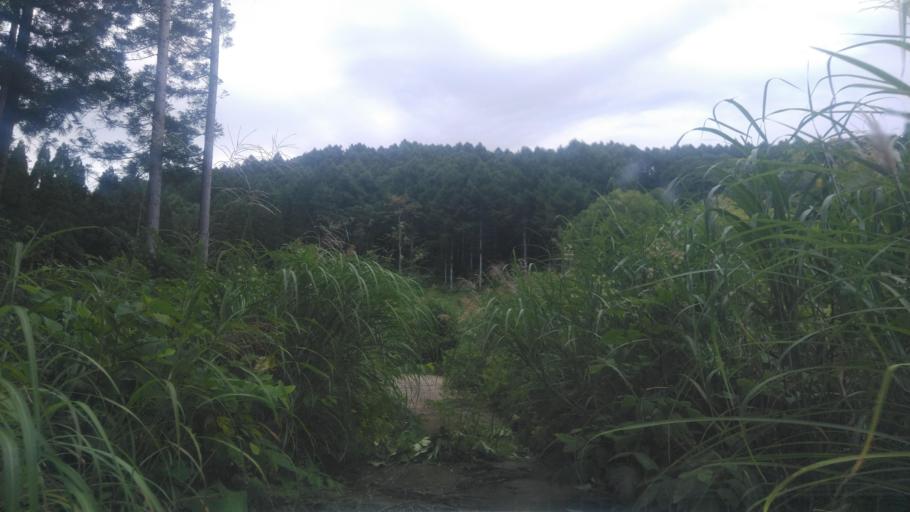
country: JP
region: Niigata
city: Arai
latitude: 36.8428
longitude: 138.1800
